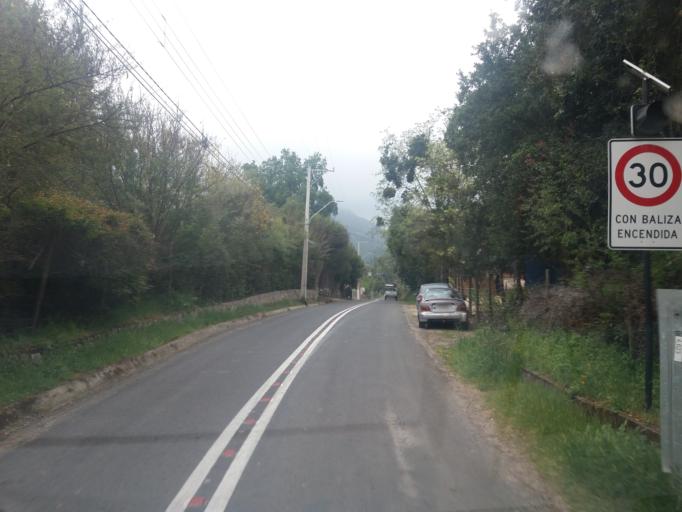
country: CL
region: Valparaiso
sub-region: Provincia de Marga Marga
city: Limache
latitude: -33.0222
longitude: -71.0719
